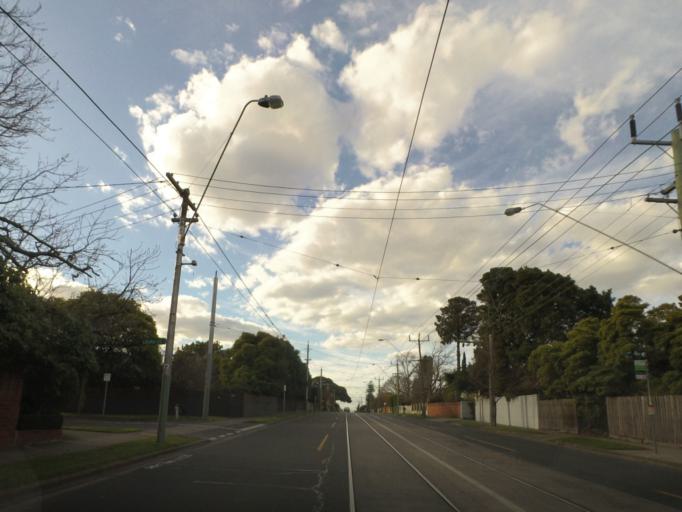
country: AU
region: Victoria
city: Glenferrie
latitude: -37.8382
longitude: 145.0553
